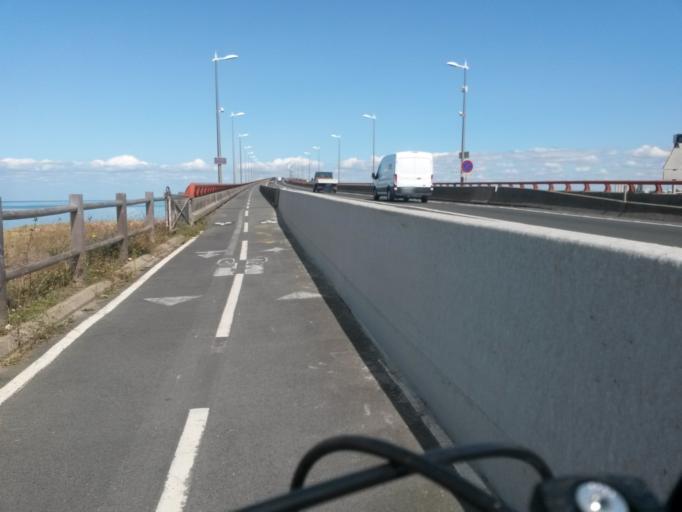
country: FR
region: Poitou-Charentes
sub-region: Departement de la Charente-Maritime
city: Rivedoux-Plage
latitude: 46.1639
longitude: -1.2562
